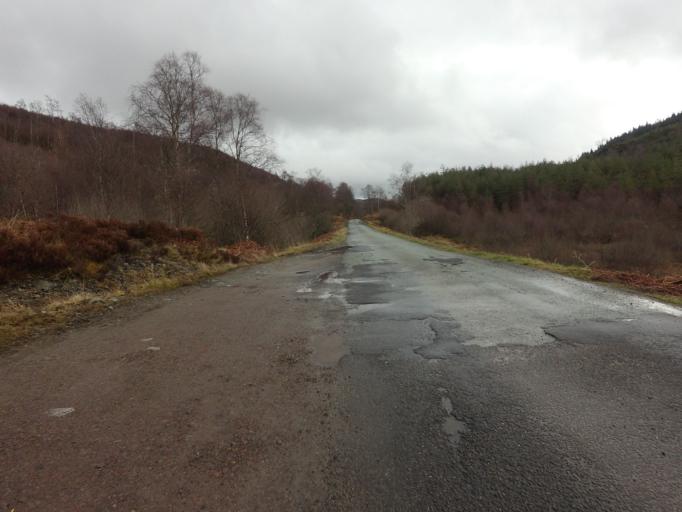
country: GB
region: Scotland
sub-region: West Dunbartonshire
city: Balloch
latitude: 56.2437
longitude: -4.5738
